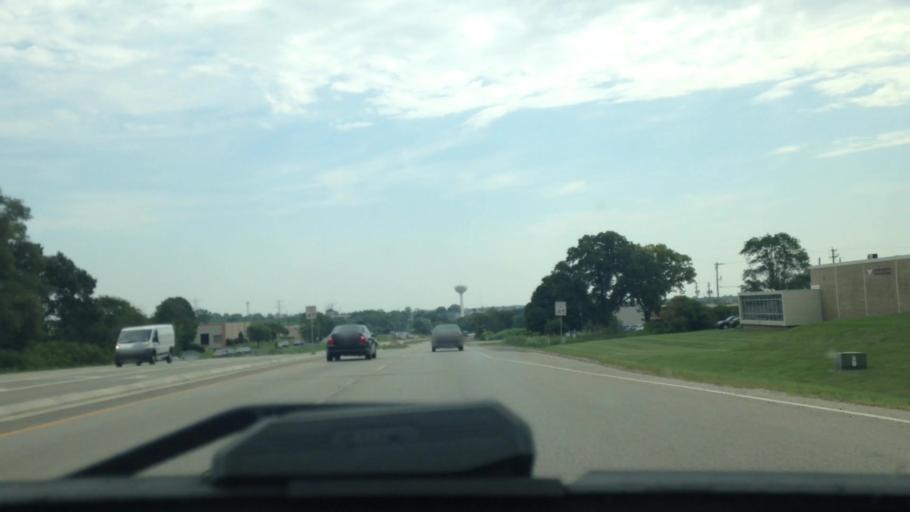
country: US
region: Wisconsin
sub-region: Waukesha County
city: Butler
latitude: 43.1190
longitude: -88.0851
